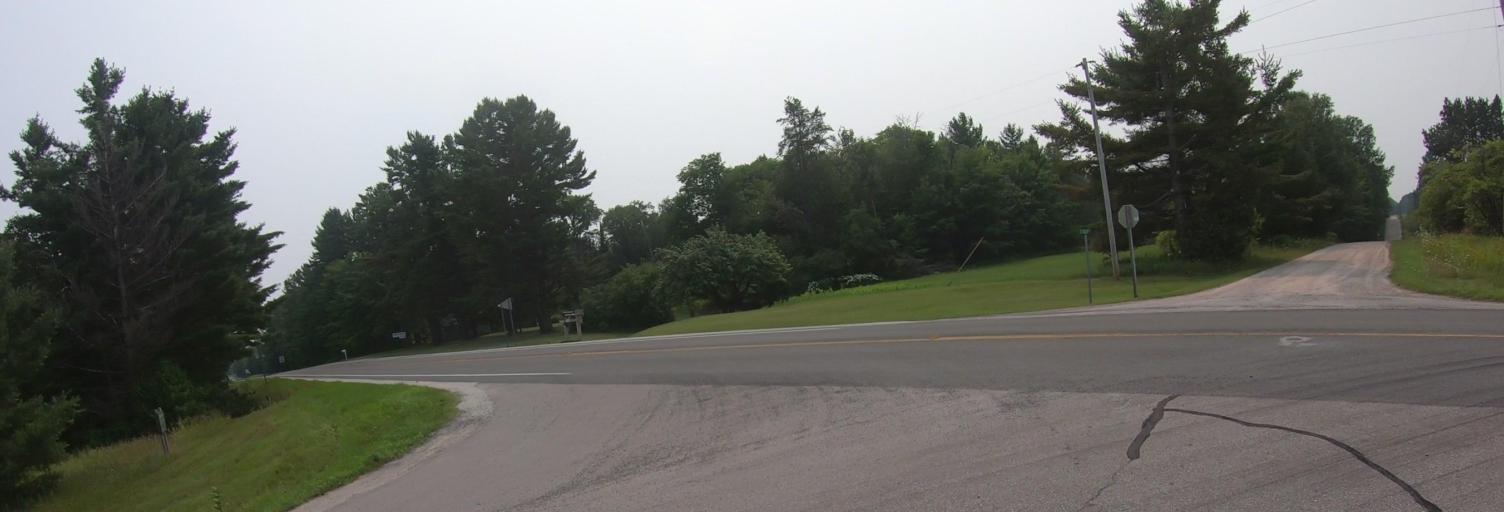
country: US
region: Michigan
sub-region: Cheboygan County
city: Cheboygan
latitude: 46.0142
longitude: -84.0711
